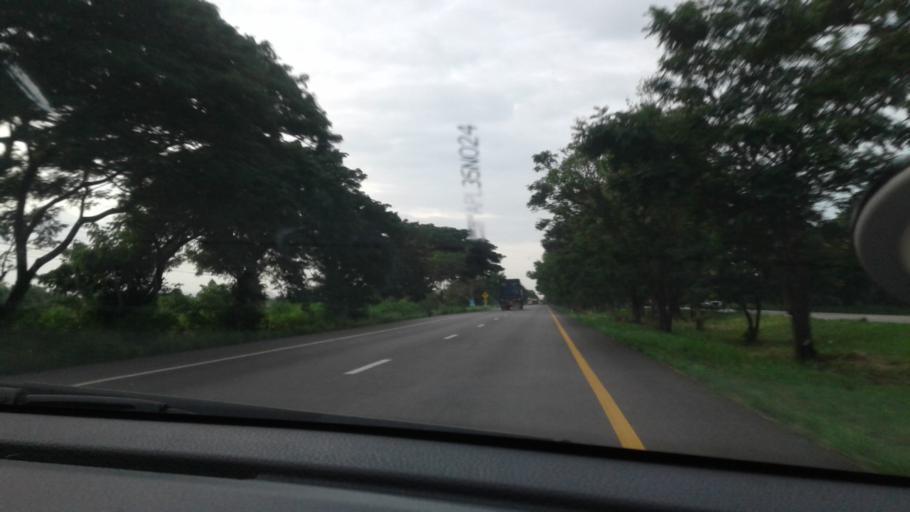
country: TH
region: Prachuap Khiri Khan
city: Pran Buri
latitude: 12.4503
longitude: 99.9041
